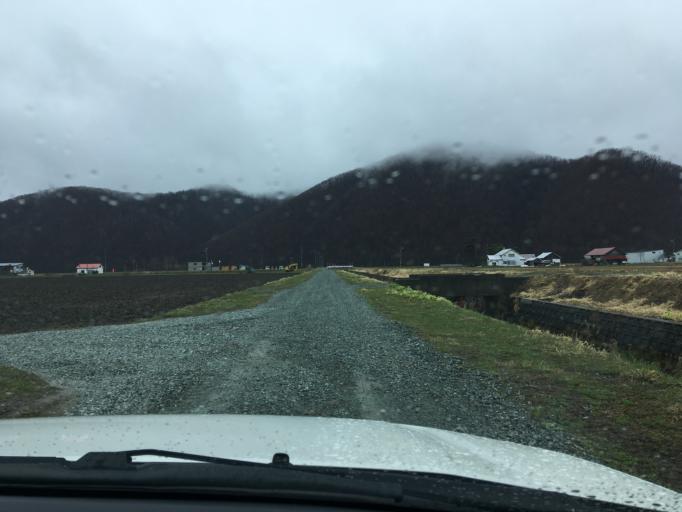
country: JP
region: Hokkaido
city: Nayoro
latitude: 44.1324
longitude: 142.4922
